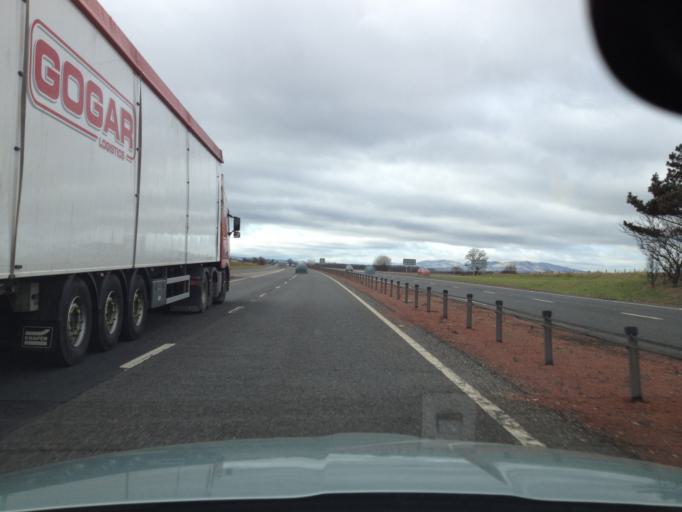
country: GB
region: Scotland
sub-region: East Lothian
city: Prestonpans
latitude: 55.9440
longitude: -2.9869
